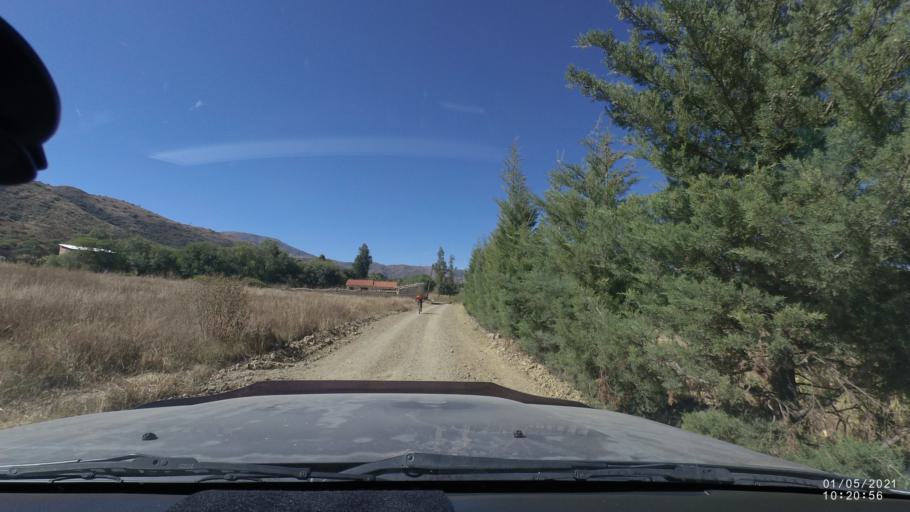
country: BO
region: Cochabamba
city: Capinota
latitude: -17.5633
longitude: -66.2032
